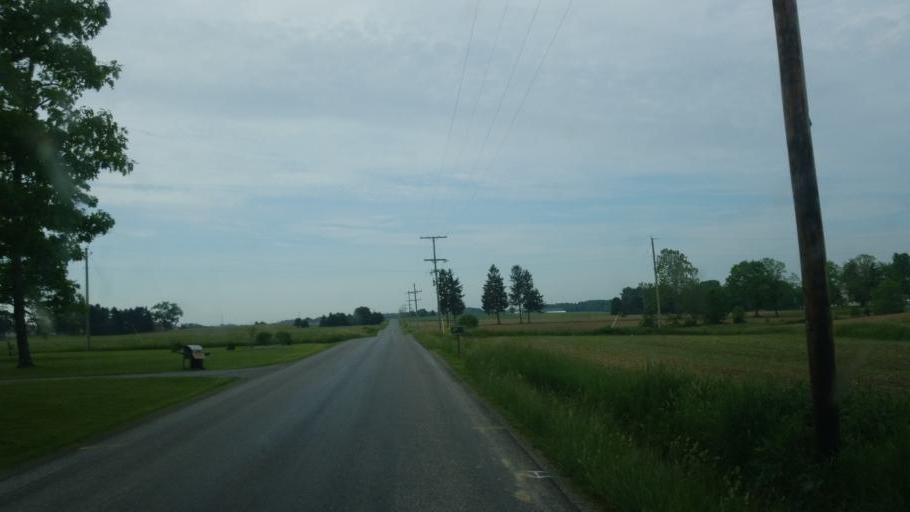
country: US
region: Ohio
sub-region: Wayne County
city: Dalton
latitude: 40.7639
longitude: -81.7550
